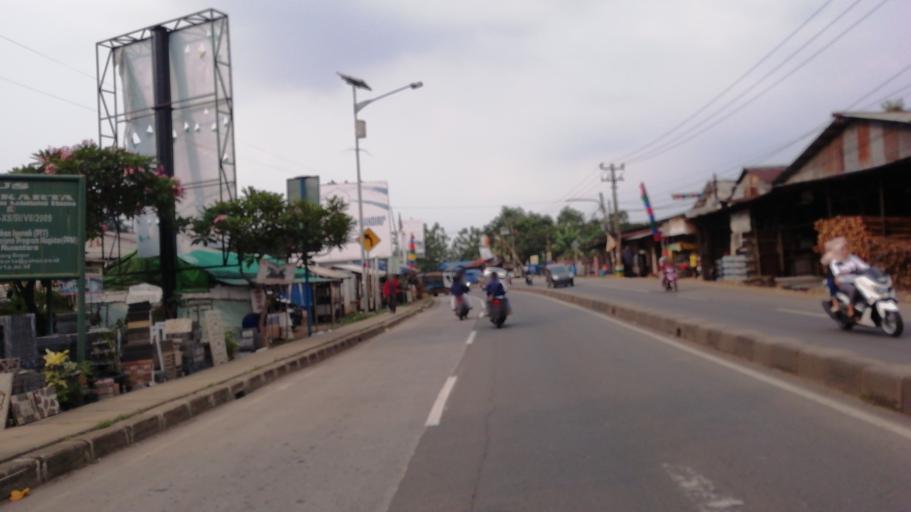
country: ID
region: West Java
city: Parung
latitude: -6.4866
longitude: 106.7361
